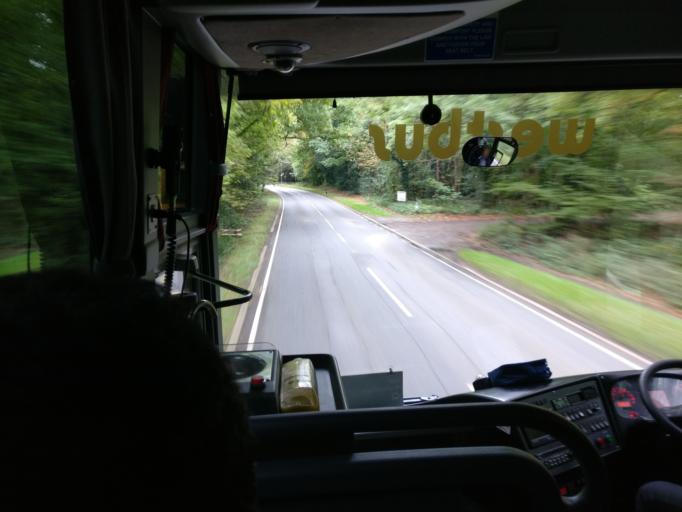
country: GB
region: England
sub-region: Surrey
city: Chobham
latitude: 51.3413
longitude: -0.5902
